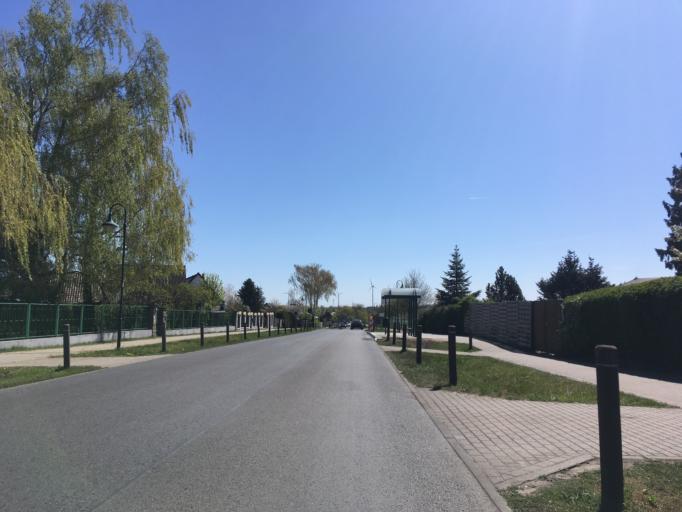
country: DE
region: Brandenburg
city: Bernau bei Berlin
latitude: 52.6427
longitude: 13.5593
